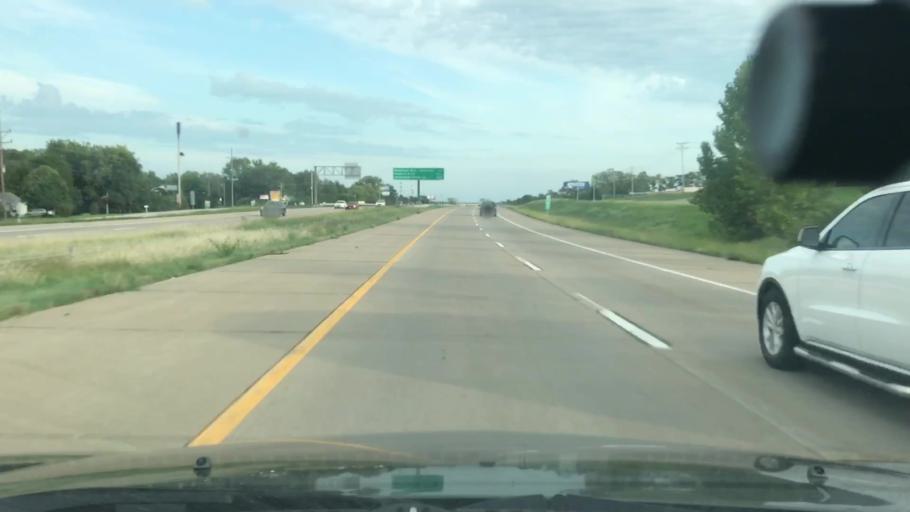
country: US
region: Missouri
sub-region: Saint Charles County
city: Dardenne Prairie
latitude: 38.7630
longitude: -90.7668
